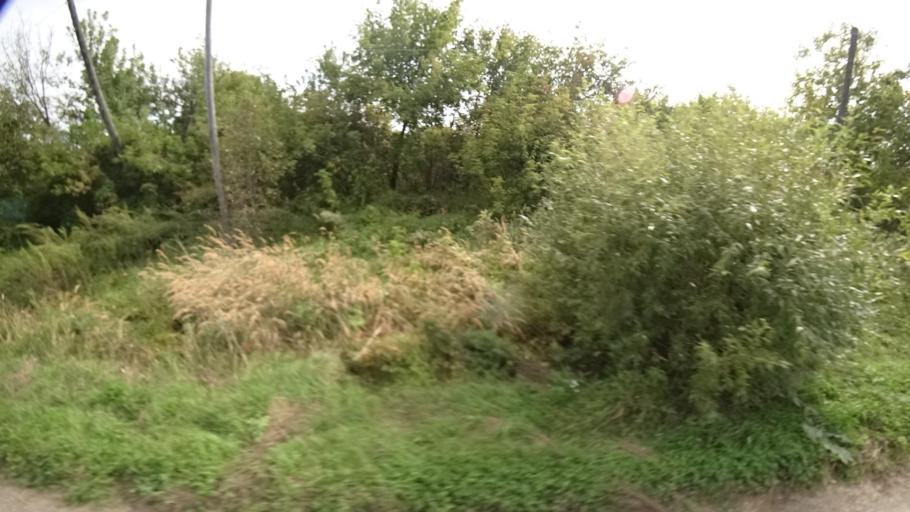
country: RU
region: Primorskiy
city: Dostoyevka
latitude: 44.3281
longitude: 133.4897
